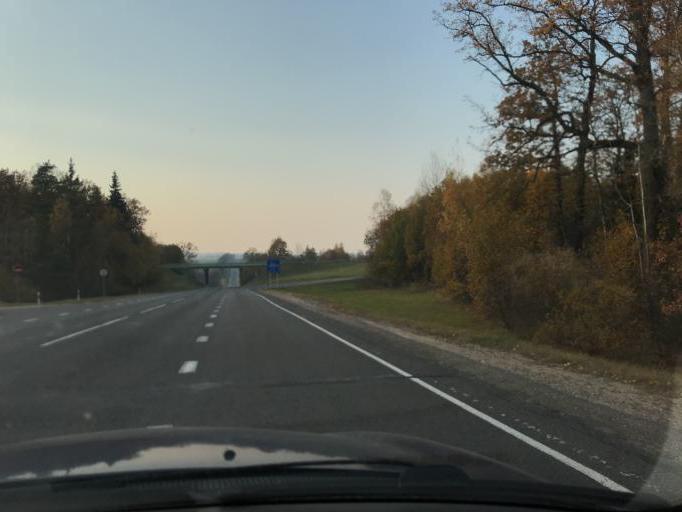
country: BY
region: Grodnenskaya
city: Navahrudak
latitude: 53.5896
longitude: 25.8871
